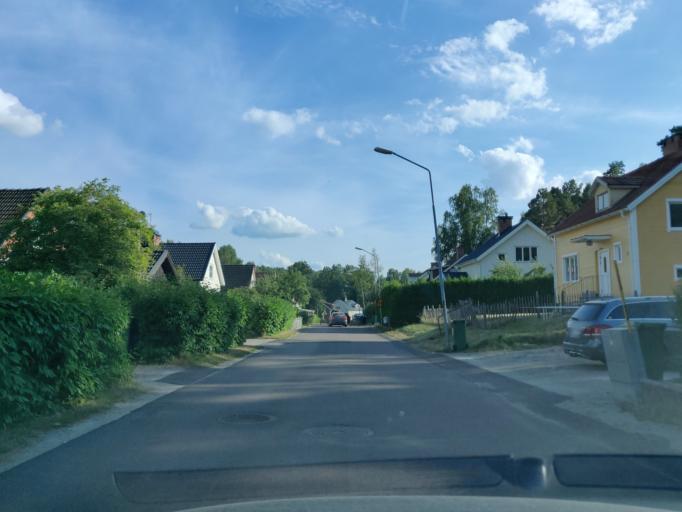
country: SE
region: Vaermland
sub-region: Hagfors Kommun
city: Hagfors
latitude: 60.0300
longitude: 13.7040
